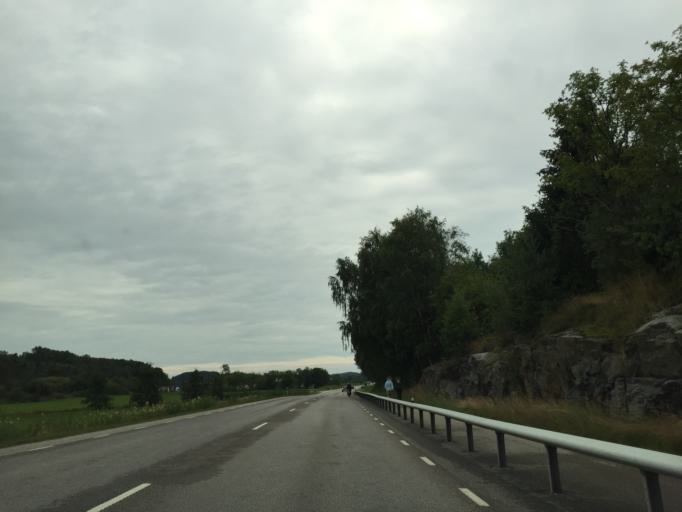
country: SE
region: Vaestra Goetaland
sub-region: Tjorns Kommun
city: Myggenas
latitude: 58.0359
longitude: 11.7293
